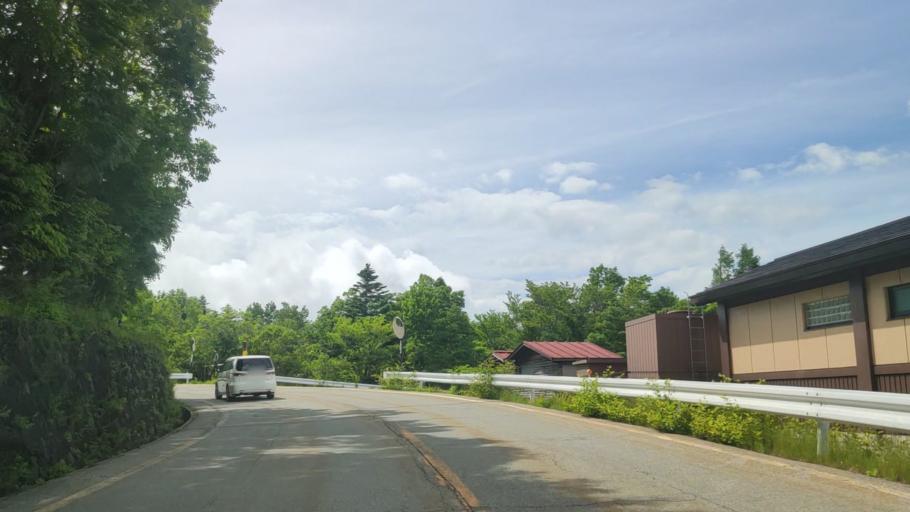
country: JP
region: Yamanashi
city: Fujikawaguchiko
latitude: 35.4152
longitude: 138.7022
